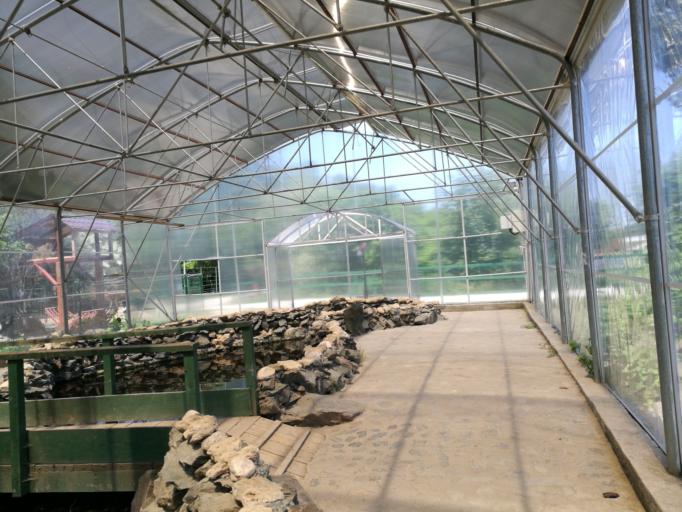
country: RO
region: Constanta
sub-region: Municipiul Constanta
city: Constanta
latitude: 44.2035
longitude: 28.6390
